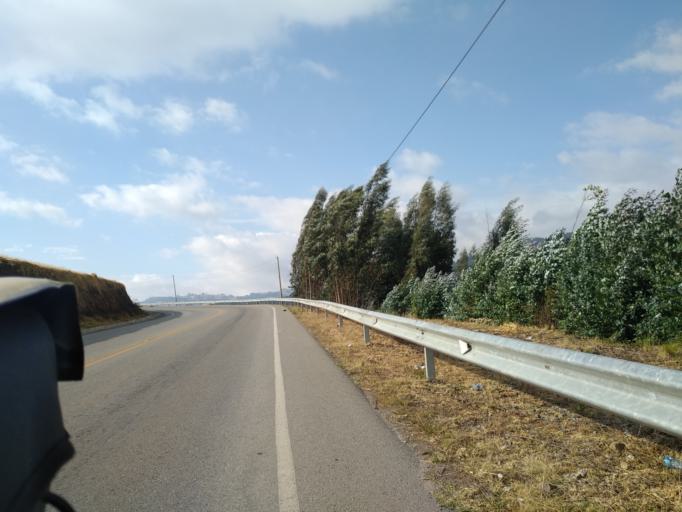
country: PE
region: La Libertad
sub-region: Provincia de Otuzco
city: Agallpampa
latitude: -7.9920
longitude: -78.5295
